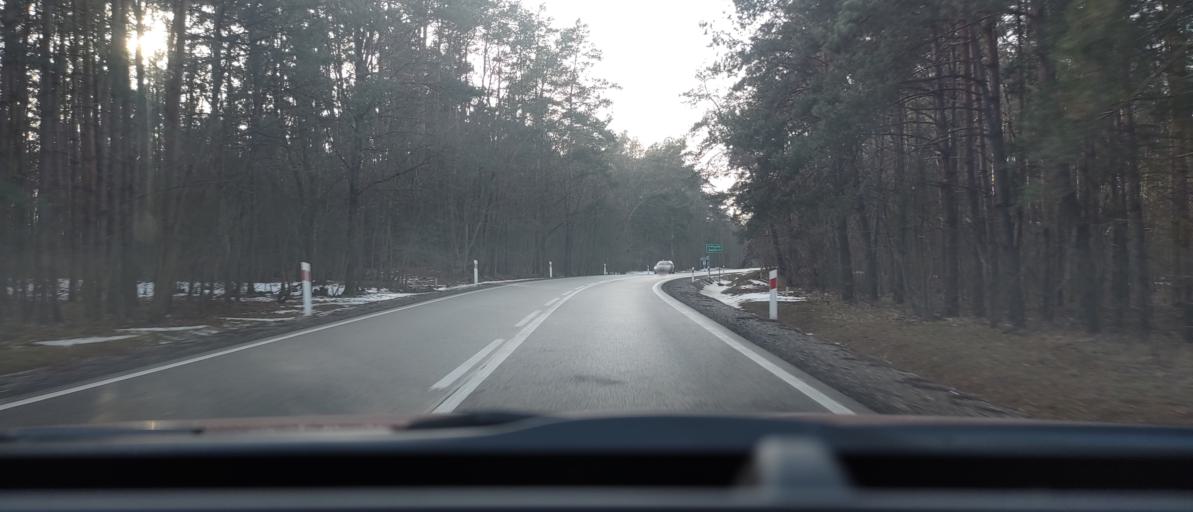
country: PL
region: Masovian Voivodeship
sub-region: Powiat bialobrzeski
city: Wysmierzyce
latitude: 51.6272
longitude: 20.8579
